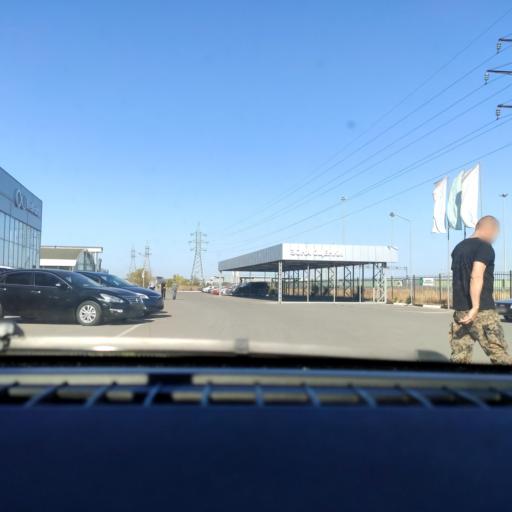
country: RU
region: Voronezj
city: Somovo
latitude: 51.6645
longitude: 39.3002
